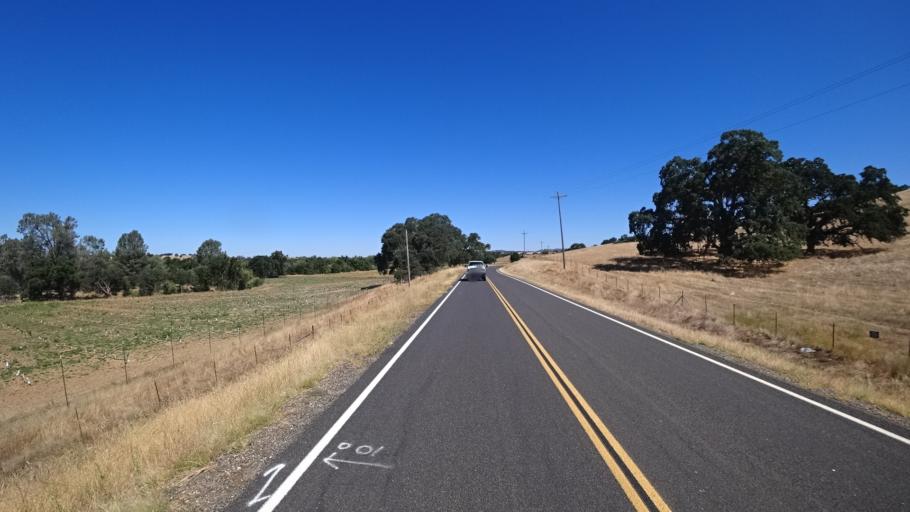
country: US
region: California
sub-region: Calaveras County
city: Rancho Calaveras
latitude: 38.0812
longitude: -120.8729
